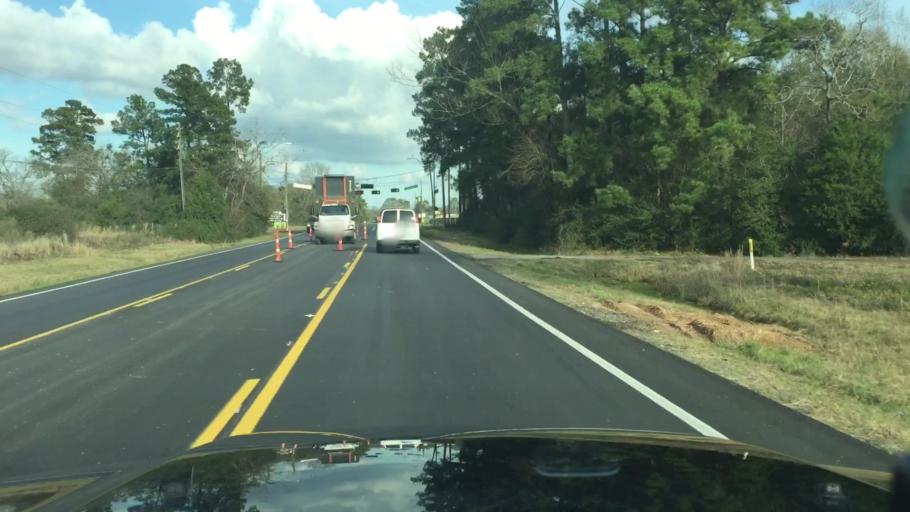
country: US
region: Texas
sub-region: Montgomery County
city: Magnolia
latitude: 30.2031
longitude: -95.7668
